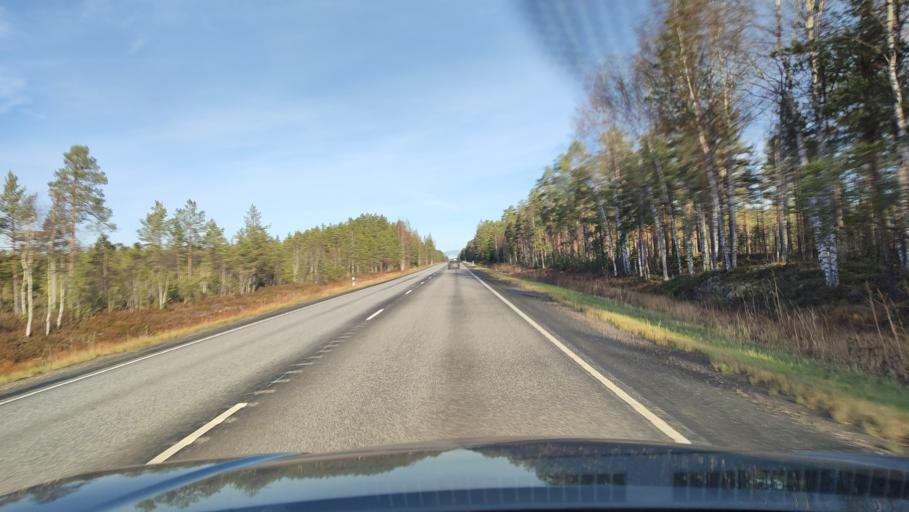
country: FI
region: Ostrobothnia
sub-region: Vaasa
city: Malax
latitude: 62.7915
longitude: 21.6709
